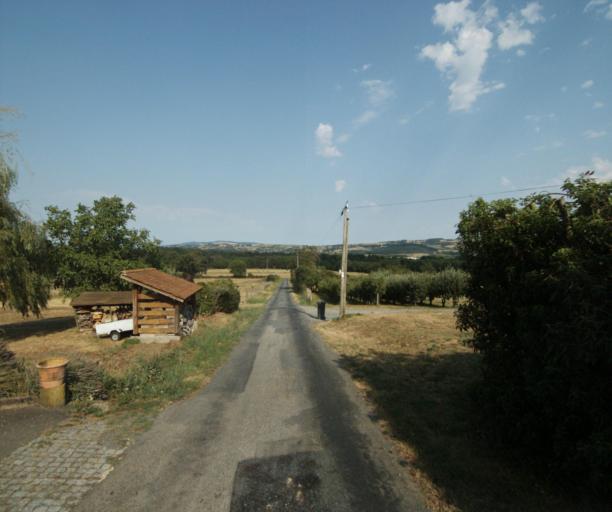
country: FR
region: Rhone-Alpes
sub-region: Departement du Rhone
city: Savigny
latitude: 45.8306
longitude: 4.5722
